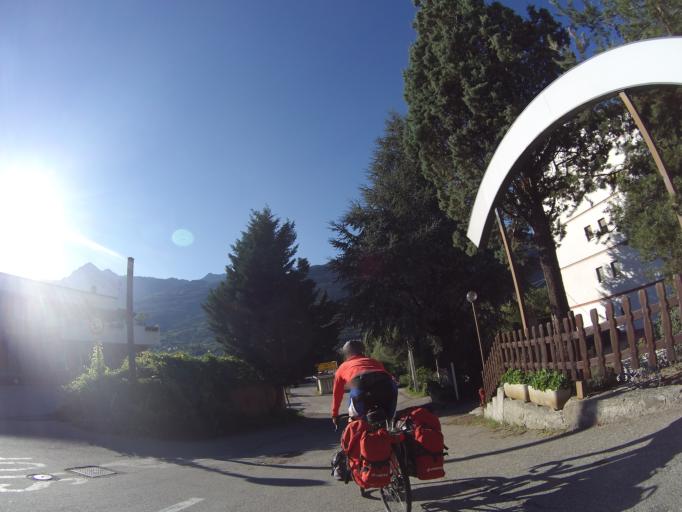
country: IT
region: Aosta Valley
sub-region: Valle d'Aosta
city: Montan-Angelin-Arensod
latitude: 45.7238
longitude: 7.2714
